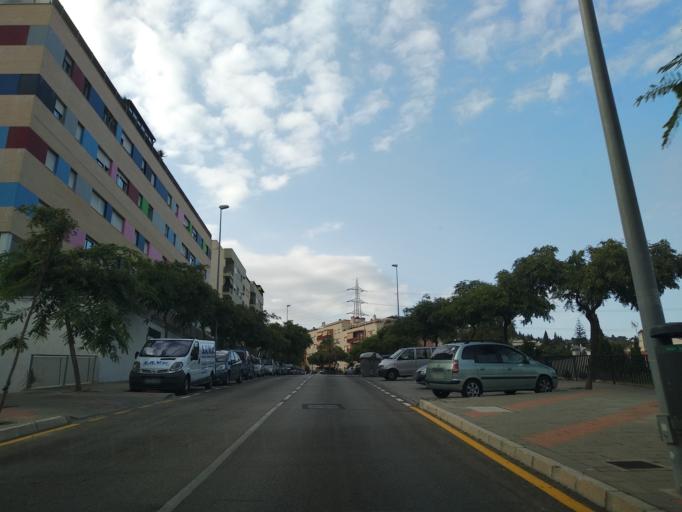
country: ES
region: Andalusia
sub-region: Provincia de Malaga
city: Malaga
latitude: 36.7304
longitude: -4.4744
